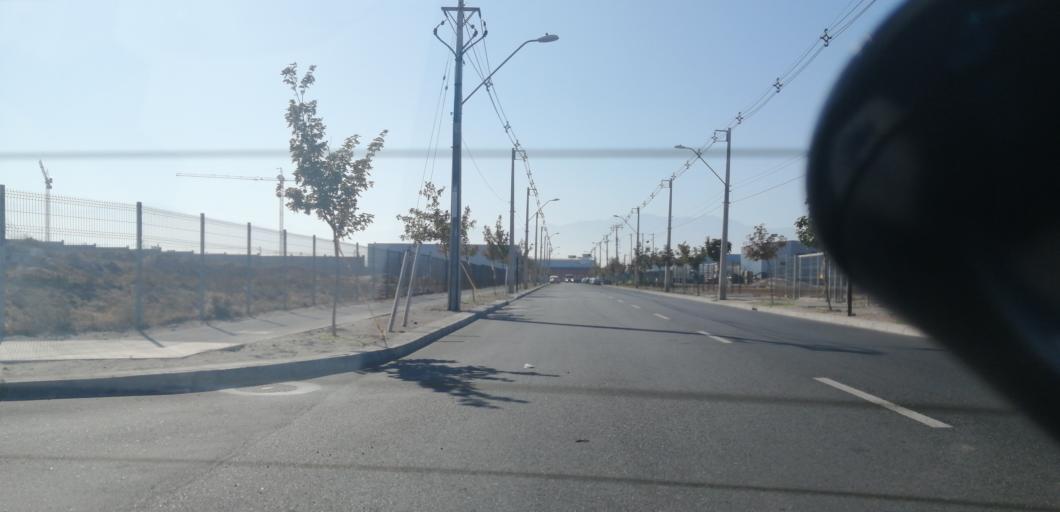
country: CL
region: Santiago Metropolitan
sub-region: Provincia de Santiago
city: Lo Prado
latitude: -33.4431
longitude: -70.7785
